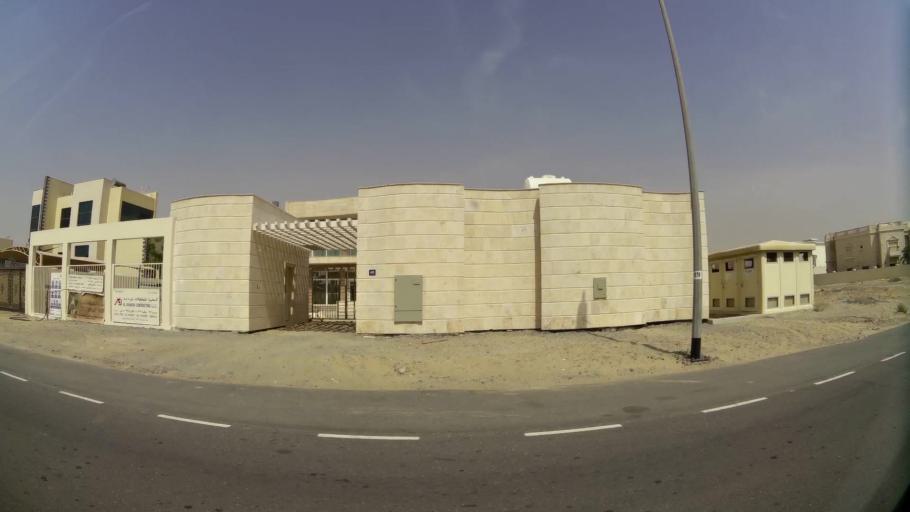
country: AE
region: Ash Shariqah
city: Sharjah
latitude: 25.2506
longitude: 55.4893
